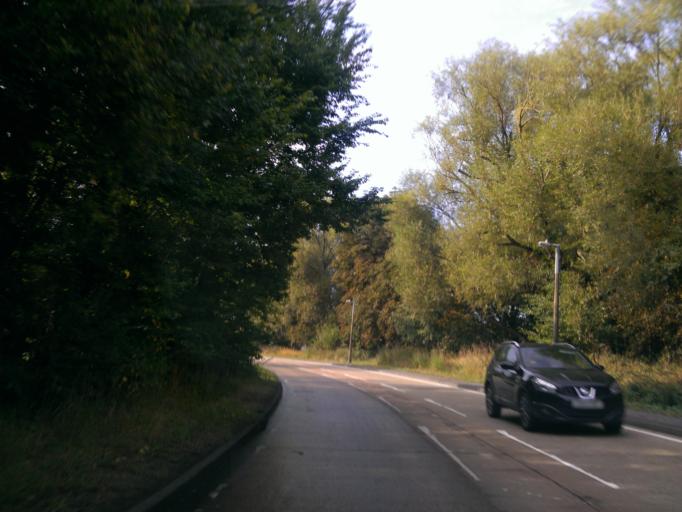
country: GB
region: England
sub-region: Essex
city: Witham
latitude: 51.8183
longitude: 0.6674
